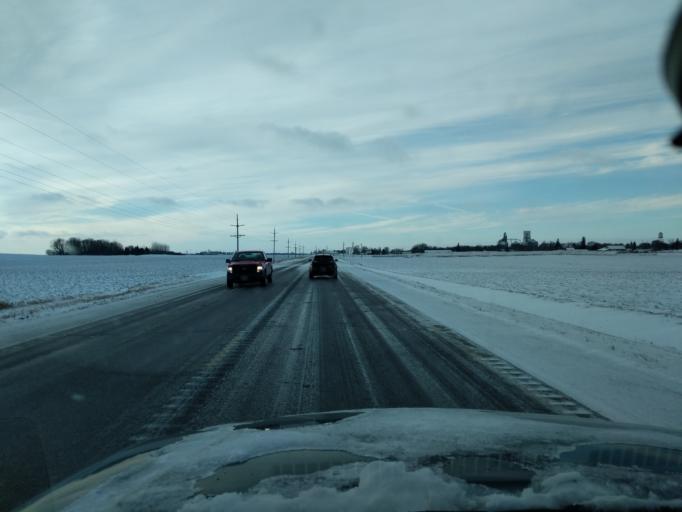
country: US
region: Minnesota
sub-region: Renville County
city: Hector
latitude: 44.7314
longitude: -94.6025
